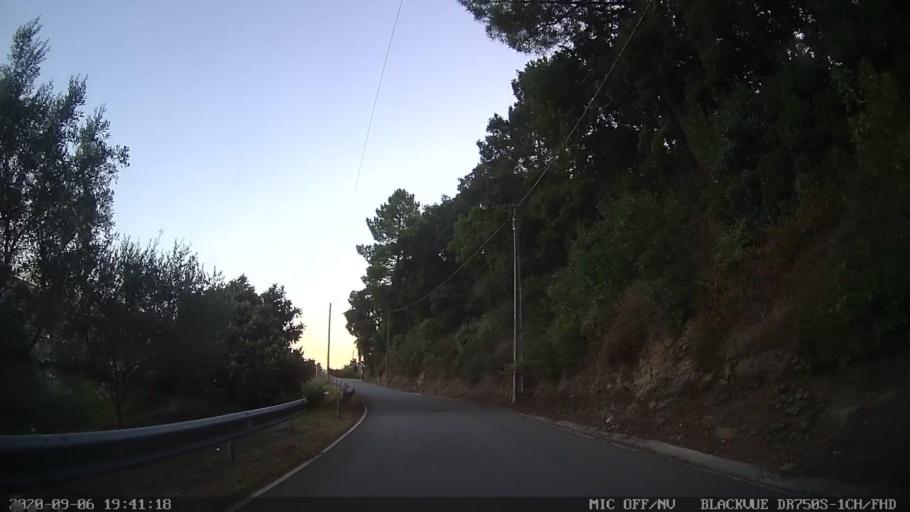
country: PT
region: Vila Real
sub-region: Mesao Frio
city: Mesao Frio
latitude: 41.1622
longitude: -7.8791
